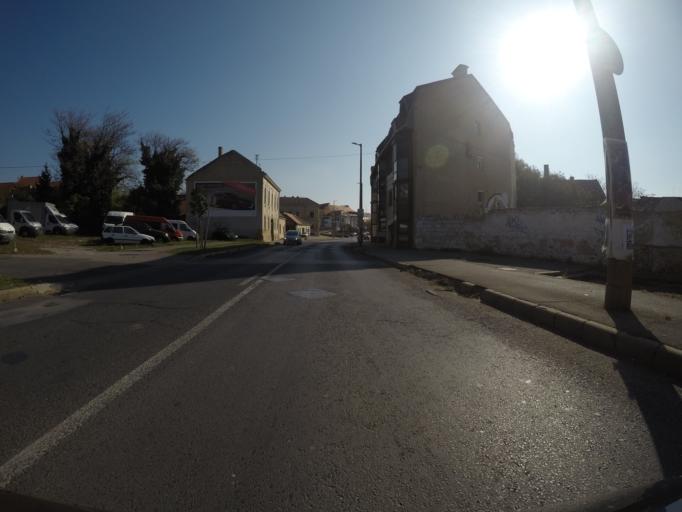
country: HU
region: Baranya
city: Pecs
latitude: 46.0782
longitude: 18.2372
